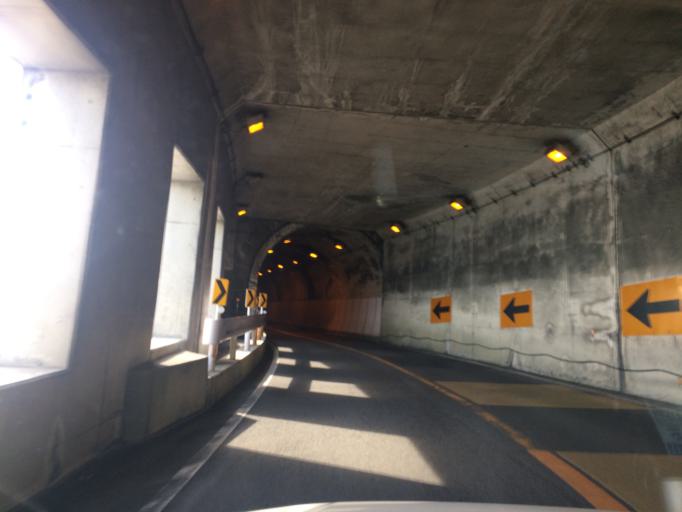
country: JP
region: Shizuoka
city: Yaizu
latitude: 34.9067
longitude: 138.3525
